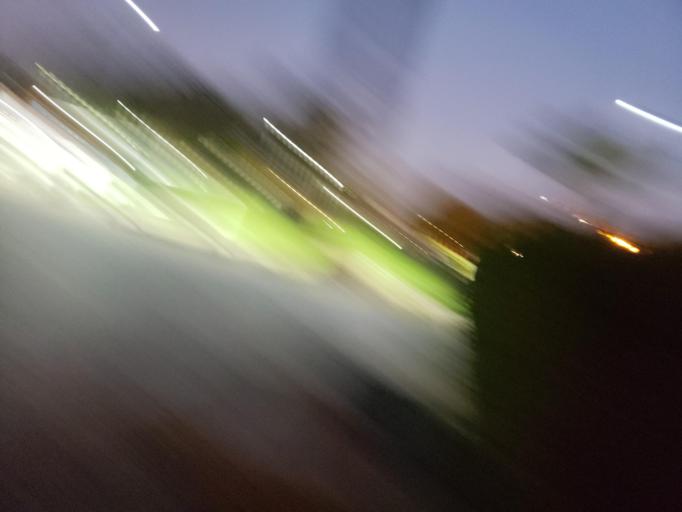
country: AE
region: Ash Shariqah
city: Sharjah
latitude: 25.3215
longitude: 55.3520
